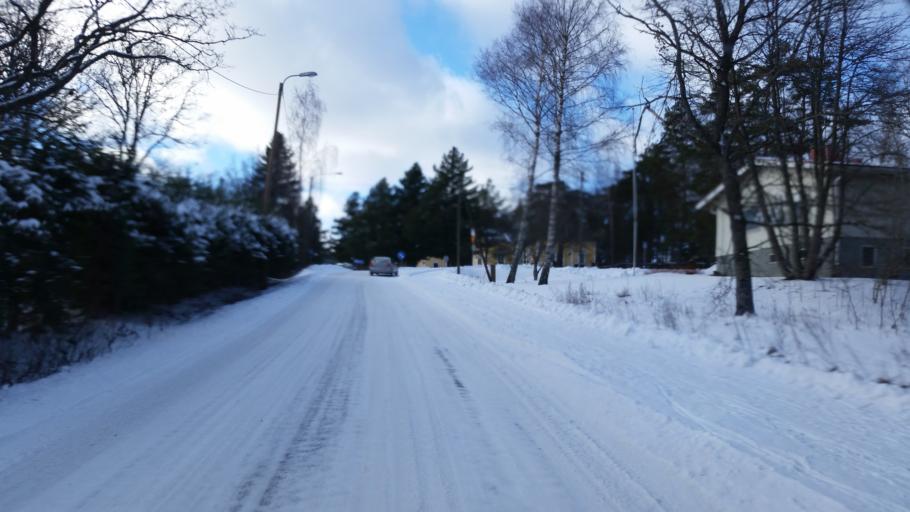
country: FI
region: Varsinais-Suomi
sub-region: Salo
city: Muurla
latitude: 60.3493
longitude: 23.2816
